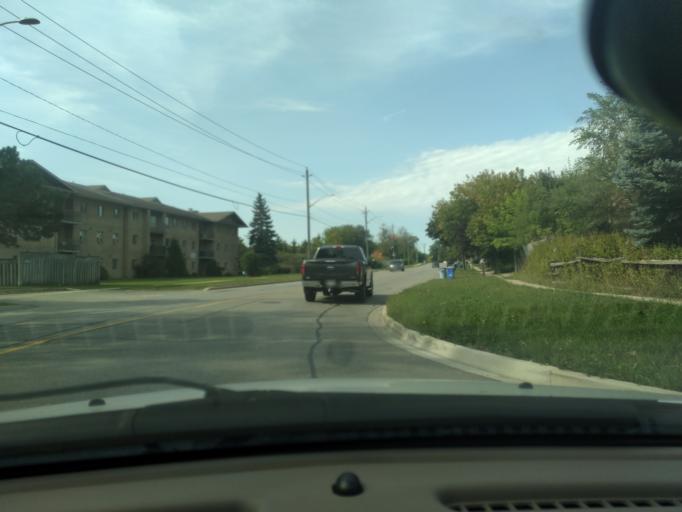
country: CA
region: Ontario
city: Barrie
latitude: 44.3833
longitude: -79.7155
